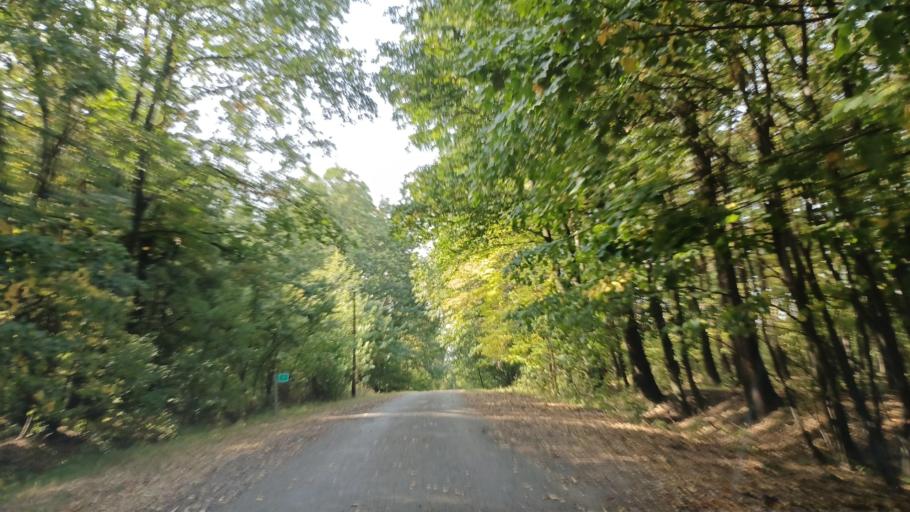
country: HU
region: Baranya
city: Mecseknadasd
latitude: 46.1973
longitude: 18.4517
